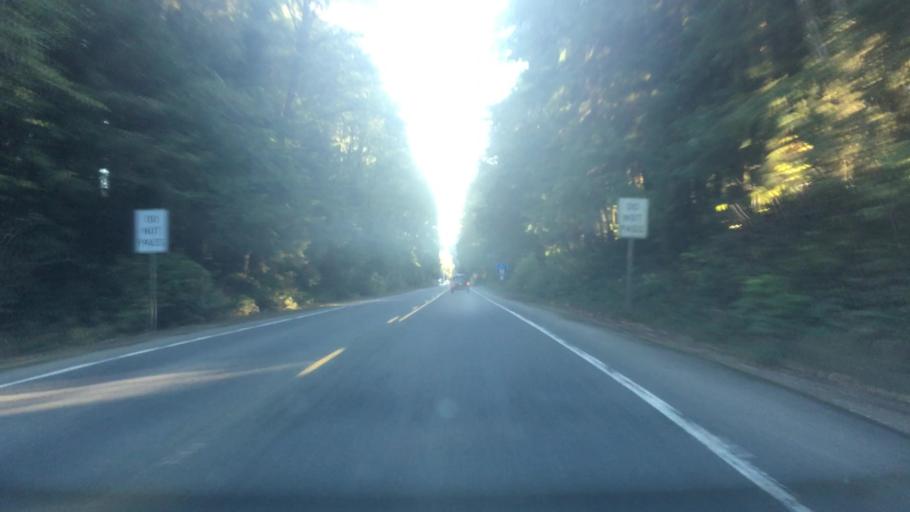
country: US
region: Oregon
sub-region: Clatsop County
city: Cannon Beach
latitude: 45.8931
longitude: -123.9562
